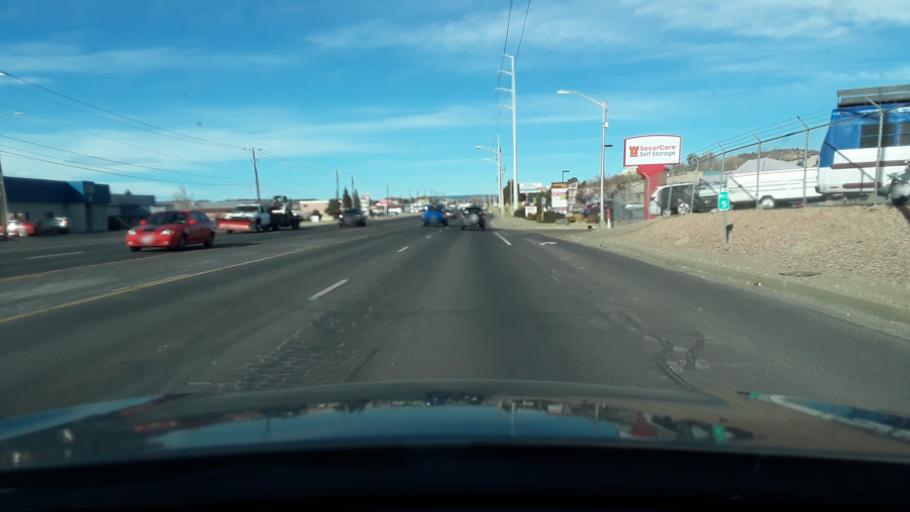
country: US
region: Colorado
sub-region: El Paso County
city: Colorado Springs
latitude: 38.8926
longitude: -104.8190
